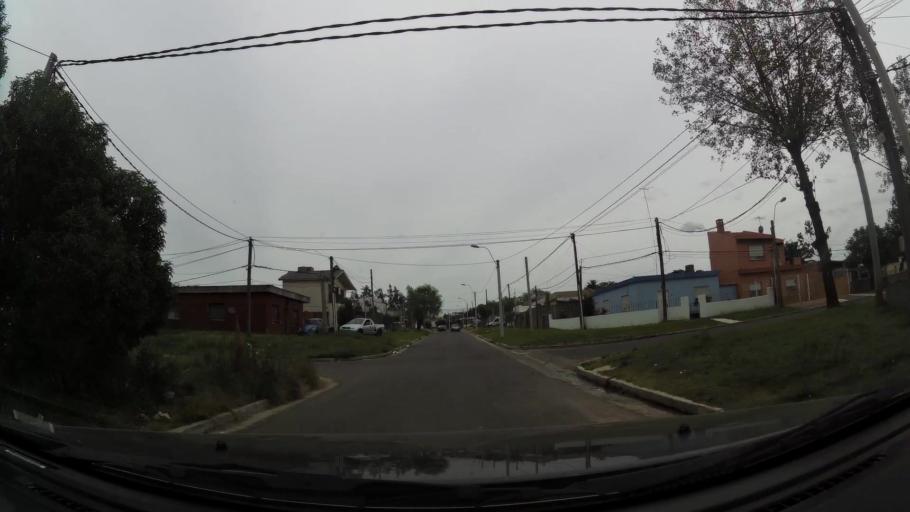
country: UY
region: Canelones
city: Las Piedras
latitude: -34.7293
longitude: -56.2086
